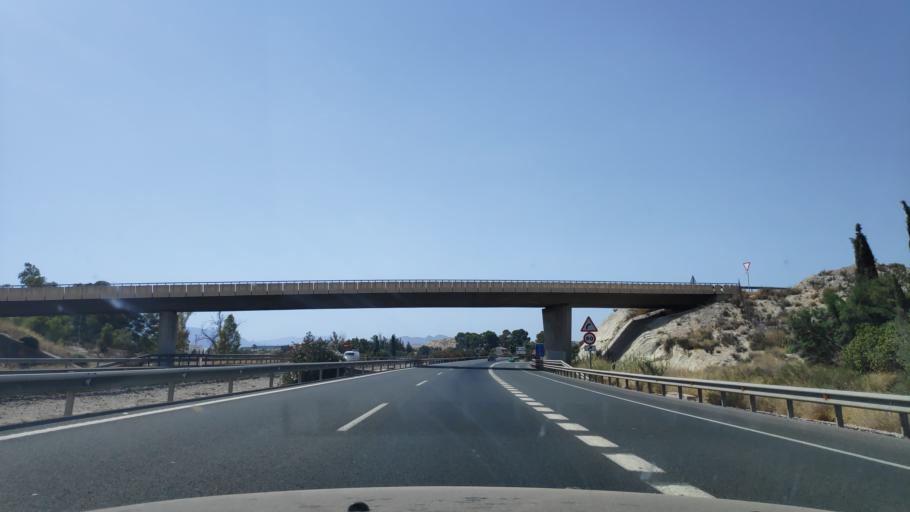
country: ES
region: Murcia
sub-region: Murcia
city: Molina de Segura
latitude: 38.0821
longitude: -1.2192
